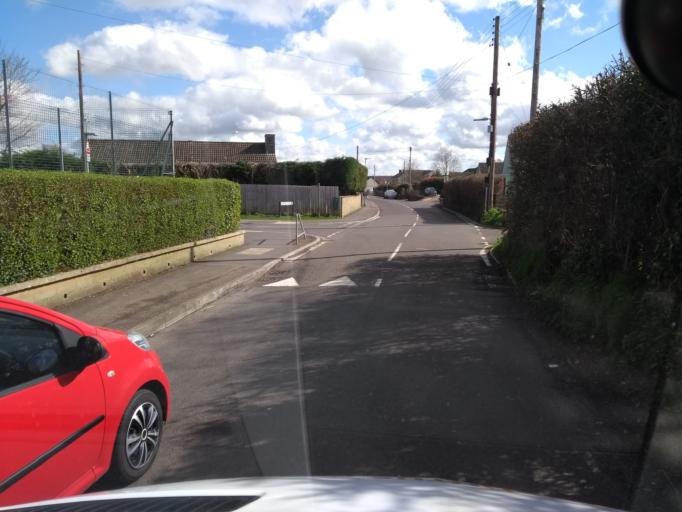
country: GB
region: England
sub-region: Somerset
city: Creech Saint Michael
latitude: 51.0276
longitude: -3.0421
